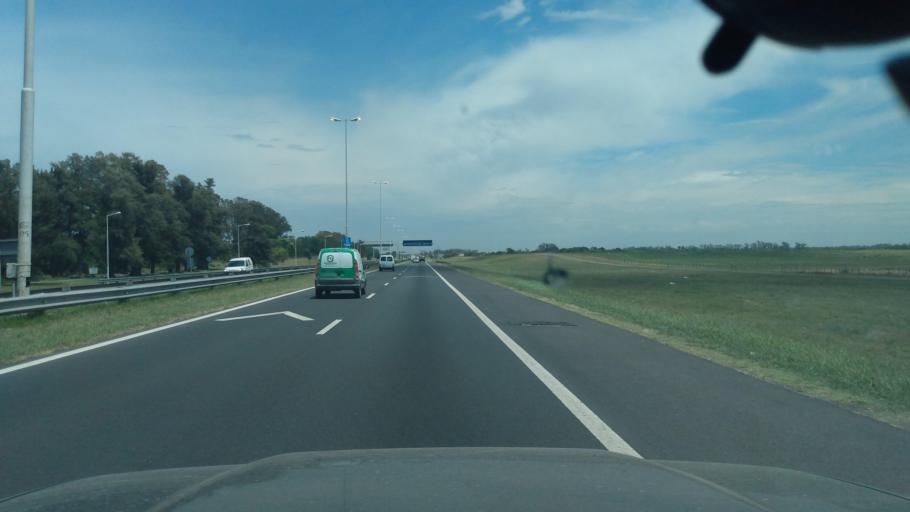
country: AR
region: Buenos Aires
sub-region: Partido de Lujan
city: Lujan
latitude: -34.5676
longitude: -59.0650
